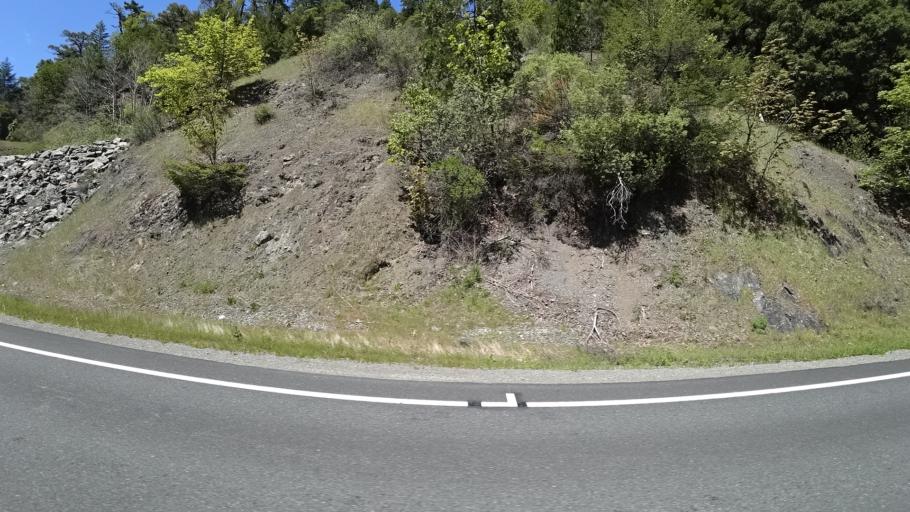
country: US
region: California
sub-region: Humboldt County
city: Willow Creek
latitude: 40.9239
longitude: -123.6923
